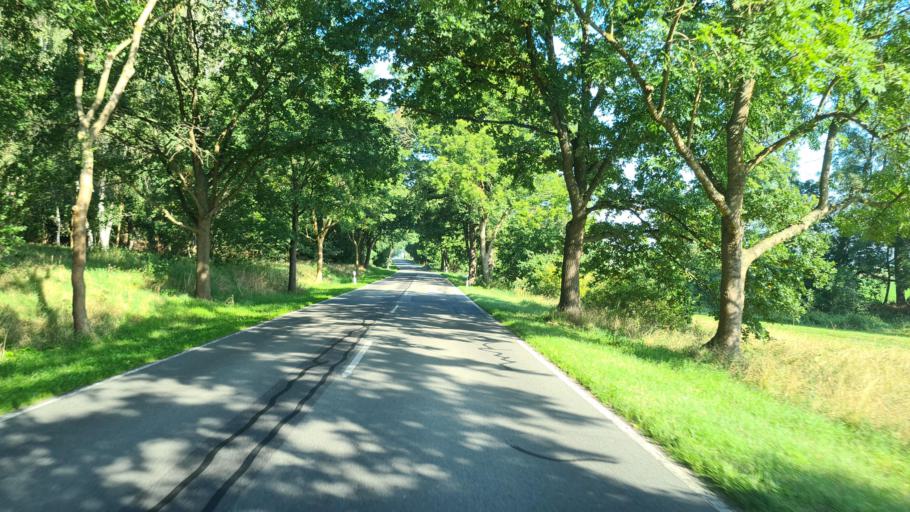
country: DE
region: Brandenburg
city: Pessin
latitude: 52.7042
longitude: 12.6459
